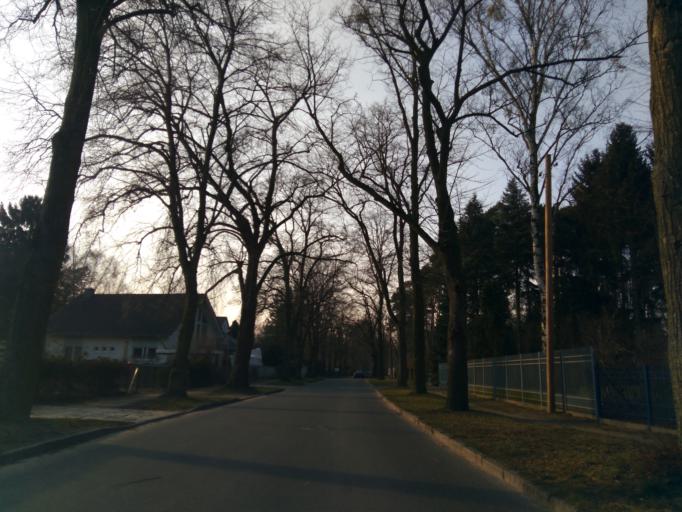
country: DE
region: Brandenburg
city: Dallgow-Doeberitz
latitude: 52.5686
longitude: 13.0641
